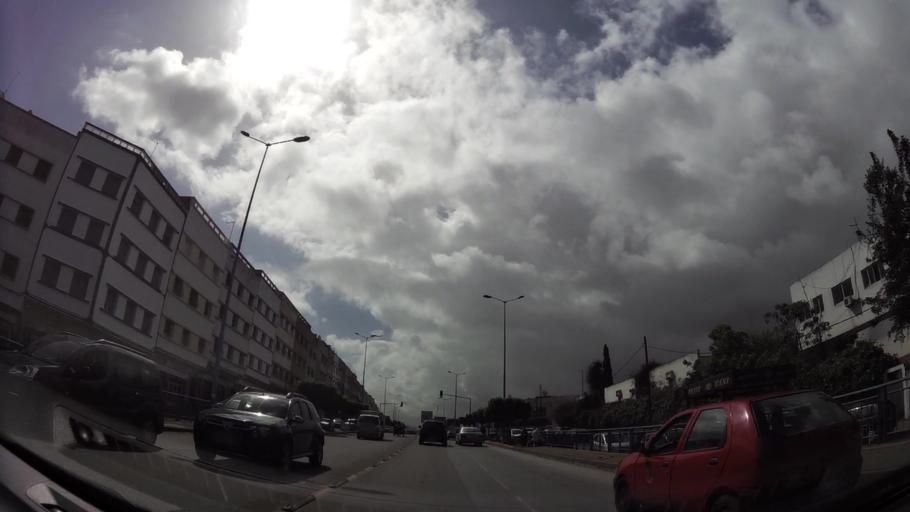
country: MA
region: Grand Casablanca
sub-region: Casablanca
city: Casablanca
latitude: 33.5591
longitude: -7.6079
